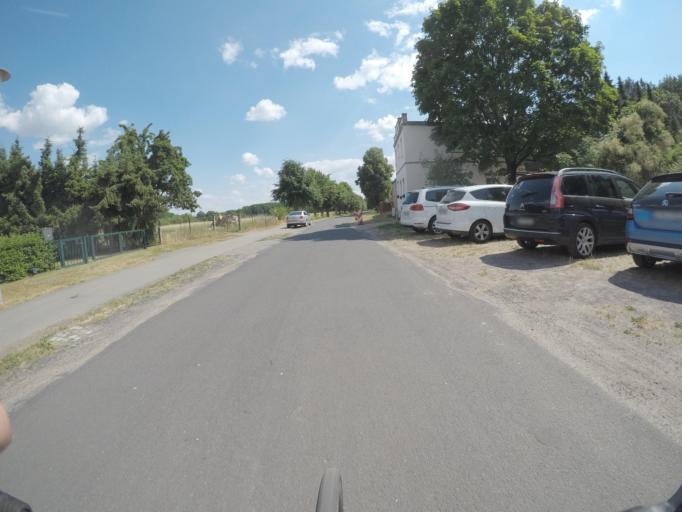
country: DE
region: Brandenburg
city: Roskow
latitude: 52.4428
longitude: 12.7345
